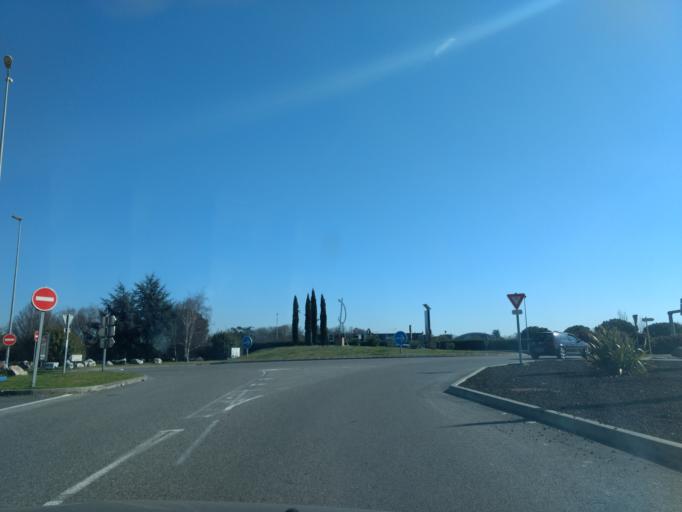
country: FR
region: Midi-Pyrenees
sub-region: Departement de la Haute-Garonne
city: Roquettes
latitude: 43.5122
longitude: 1.3692
